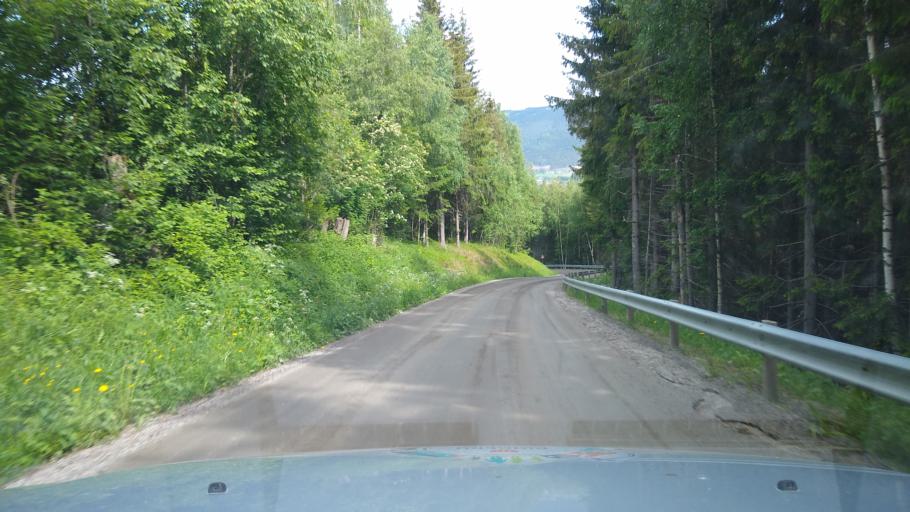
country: NO
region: Oppland
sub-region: Ringebu
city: Ringebu
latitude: 61.5183
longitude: 10.1311
